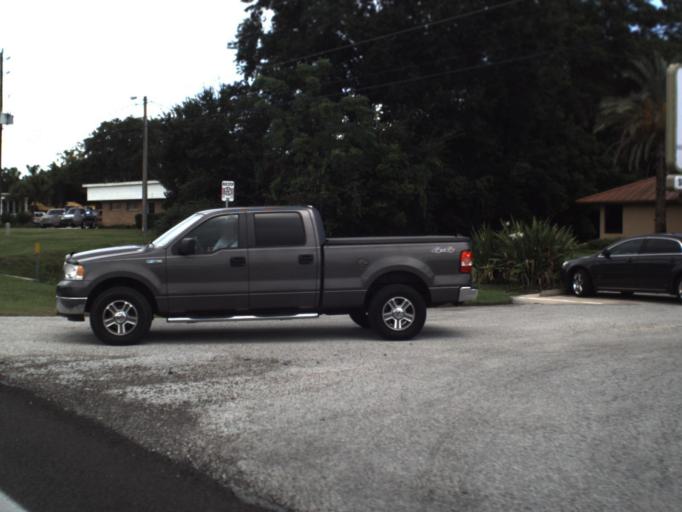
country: US
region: Florida
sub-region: Polk County
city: Medulla
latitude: 27.9638
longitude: -81.9657
